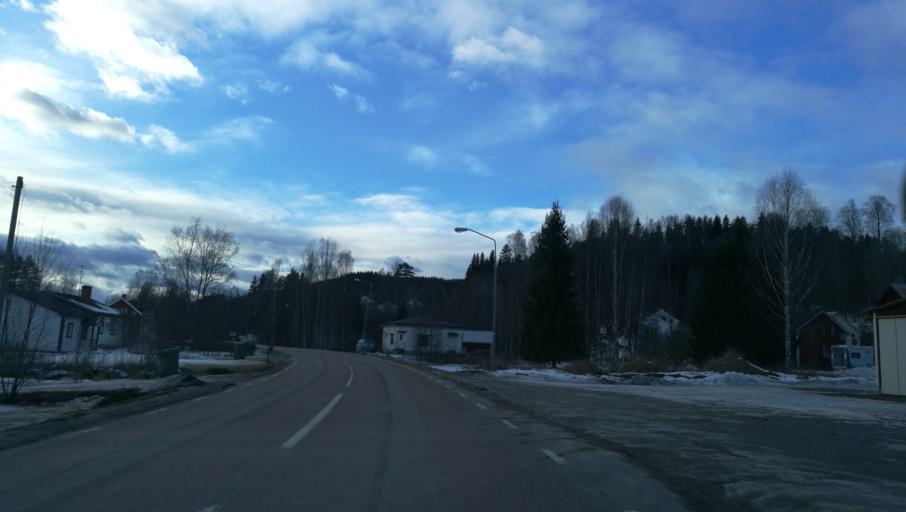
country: SE
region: Vaermland
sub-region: Torsby Kommun
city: Torsby
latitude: 60.7370
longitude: 12.8627
